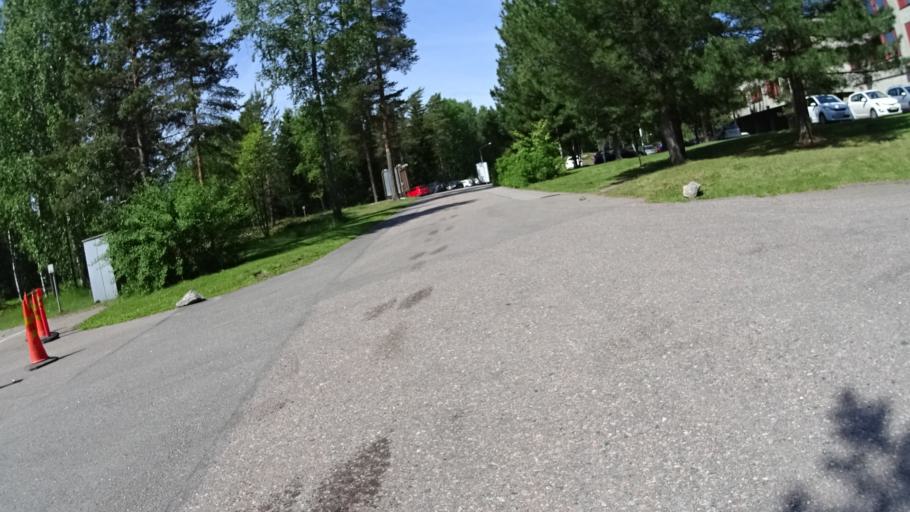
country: FI
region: Uusimaa
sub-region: Helsinki
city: Kauniainen
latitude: 60.3245
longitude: 24.7308
